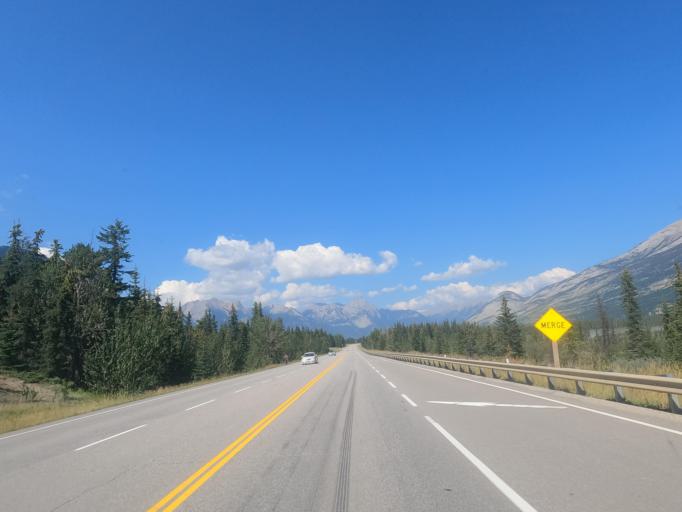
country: CA
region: Alberta
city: Jasper Park Lodge
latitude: 52.9634
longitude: -118.0515
